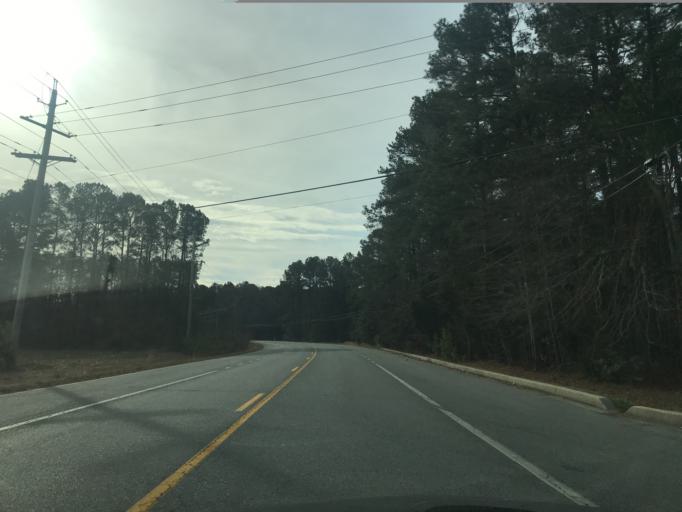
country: US
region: Maryland
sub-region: Charles County
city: Cobb Island
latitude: 38.2936
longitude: -76.8799
